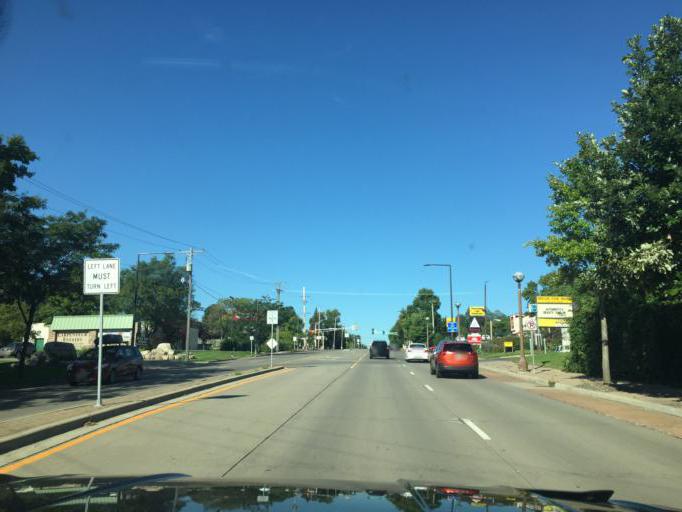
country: US
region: Minnesota
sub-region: Ramsey County
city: Falcon Heights
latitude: 44.9919
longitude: -93.1541
